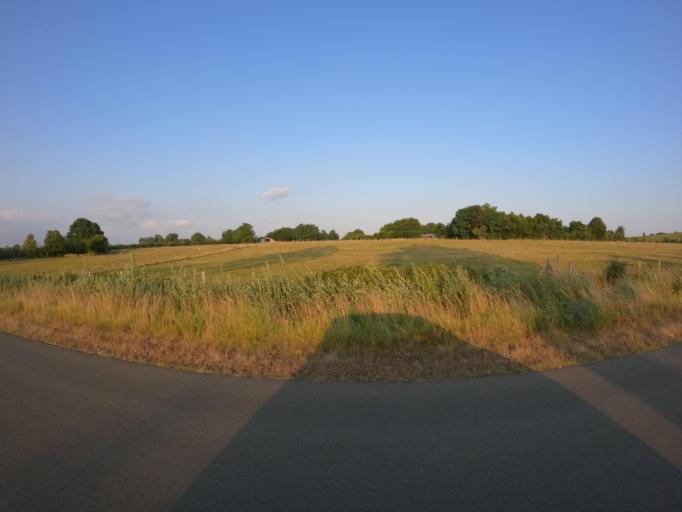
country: FR
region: Pays de la Loire
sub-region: Departement de la Sarthe
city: Brulon
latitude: 47.9124
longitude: -0.2290
